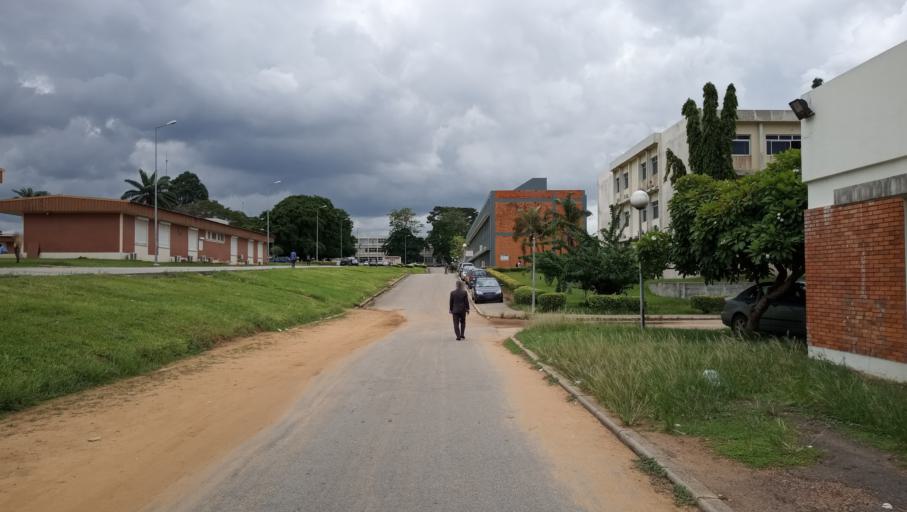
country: CI
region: Lagunes
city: Abidjan
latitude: 5.3407
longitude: -3.9864
